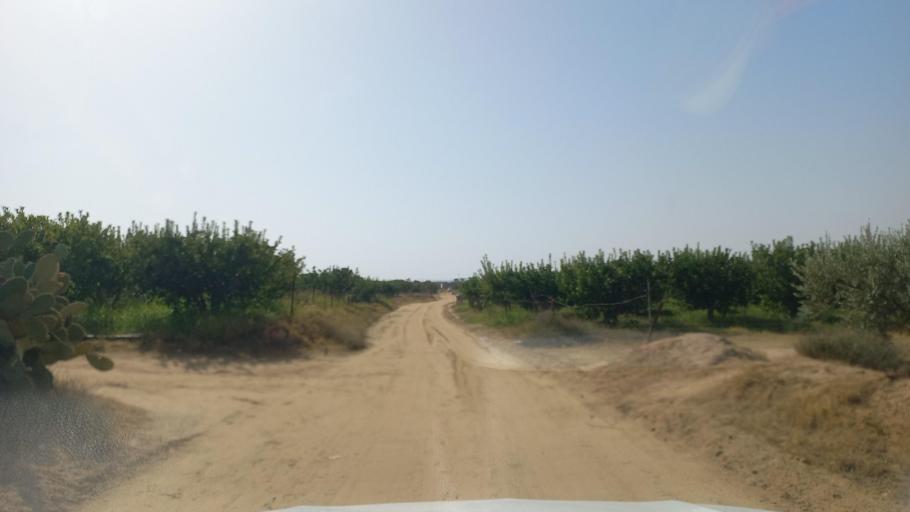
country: TN
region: Al Qasrayn
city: Kasserine
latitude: 35.2438
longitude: 9.0340
